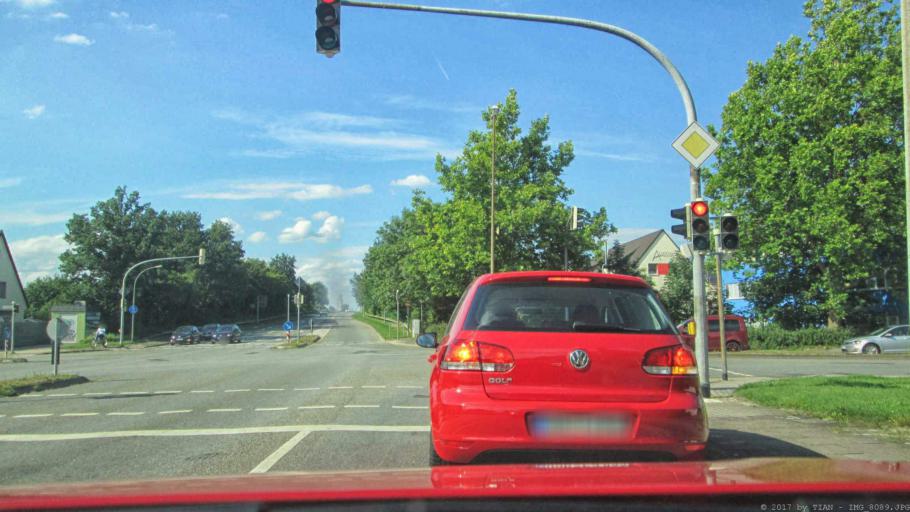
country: DE
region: Lower Saxony
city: Weyhausen
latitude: 52.4206
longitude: 10.7117
